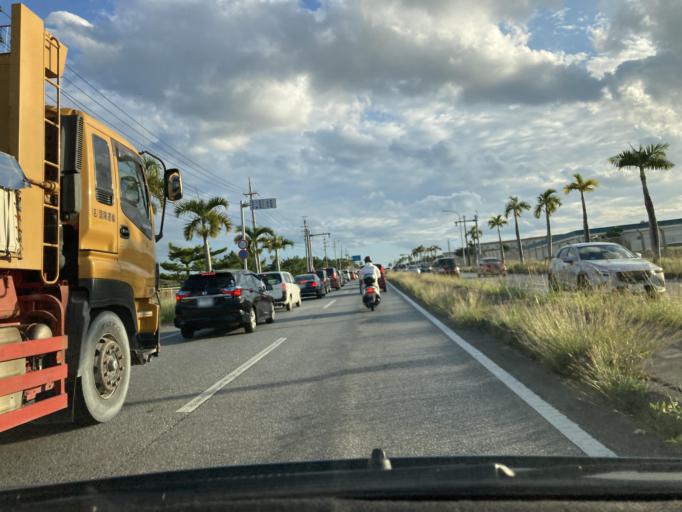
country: JP
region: Okinawa
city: Chatan
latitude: 26.3012
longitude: 127.7805
